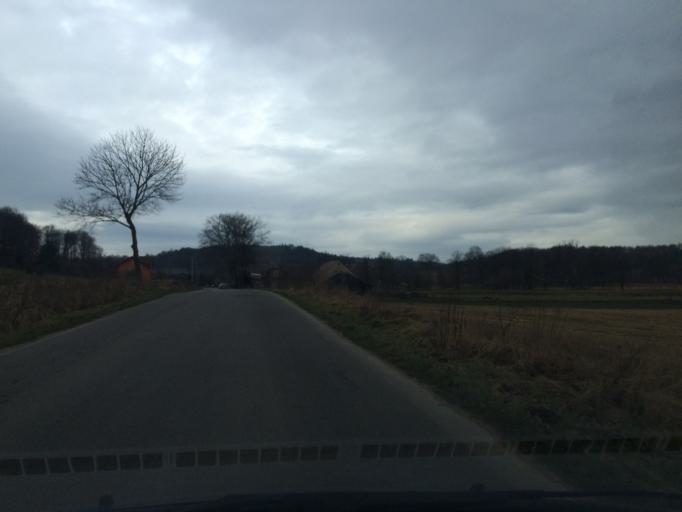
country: PL
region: Lower Silesian Voivodeship
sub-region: Powiat lwowecki
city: Lwowek Slaski
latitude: 51.1195
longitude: 15.5521
